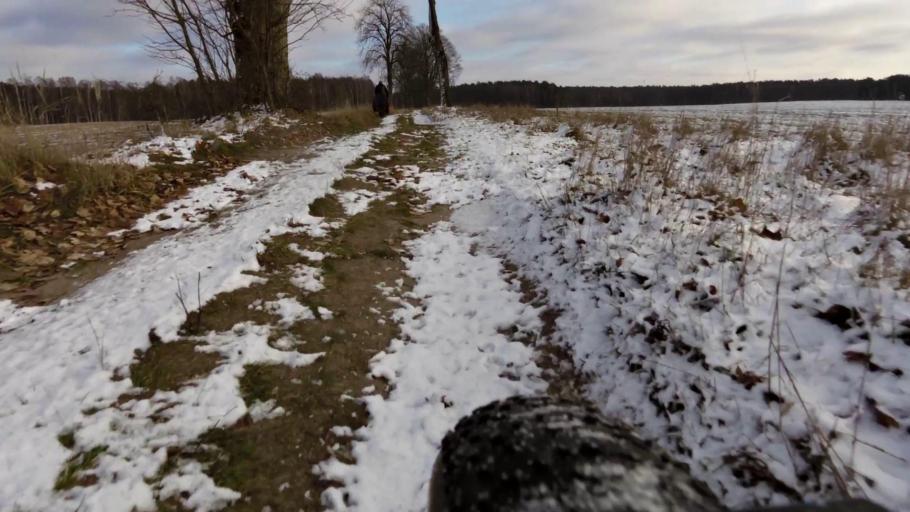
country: PL
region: West Pomeranian Voivodeship
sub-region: Powiat walecki
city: Tuczno
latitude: 53.3010
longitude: 16.2777
